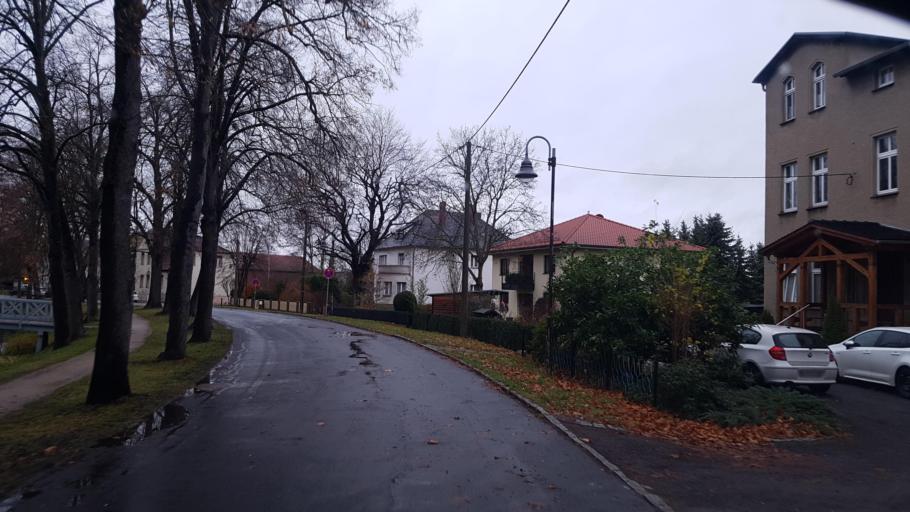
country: DE
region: Brandenburg
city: Luckau
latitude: 51.8539
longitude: 13.7176
